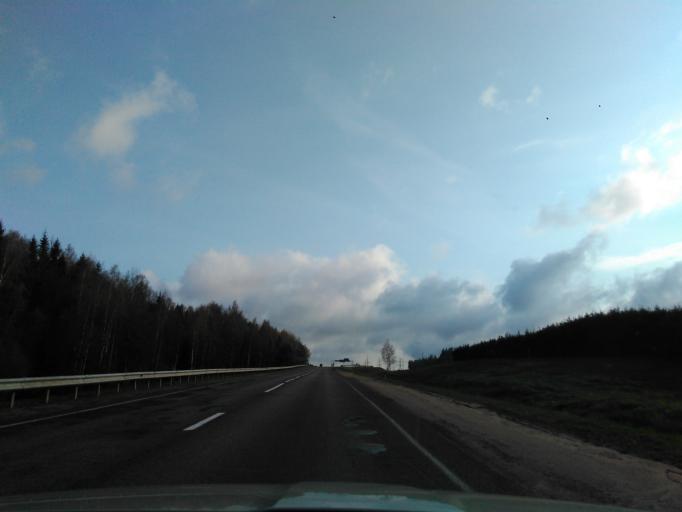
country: BY
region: Minsk
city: Lahoysk
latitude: 54.2140
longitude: 27.8280
